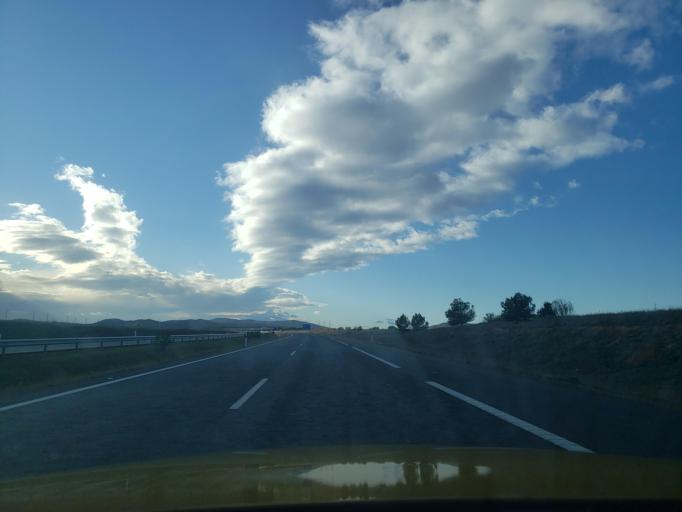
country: ES
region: Castille-La Mancha
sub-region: Province of Toledo
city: Consuegra
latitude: 39.4768
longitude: -3.6036
